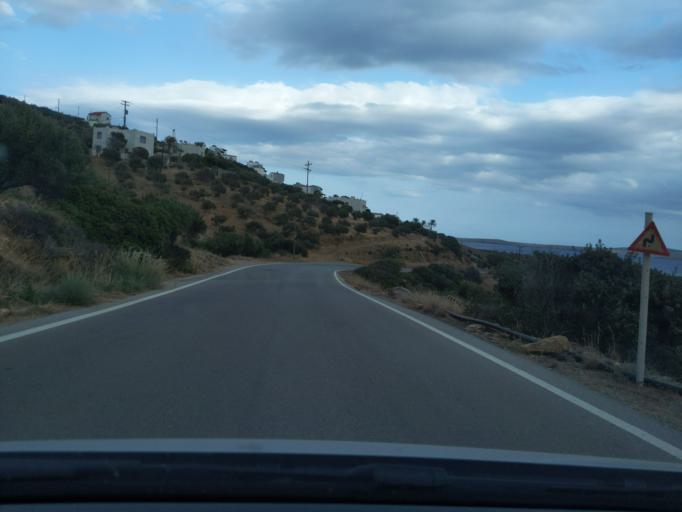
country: GR
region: Crete
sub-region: Nomos Lasithiou
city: Palekastro
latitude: 35.2182
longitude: 26.2607
